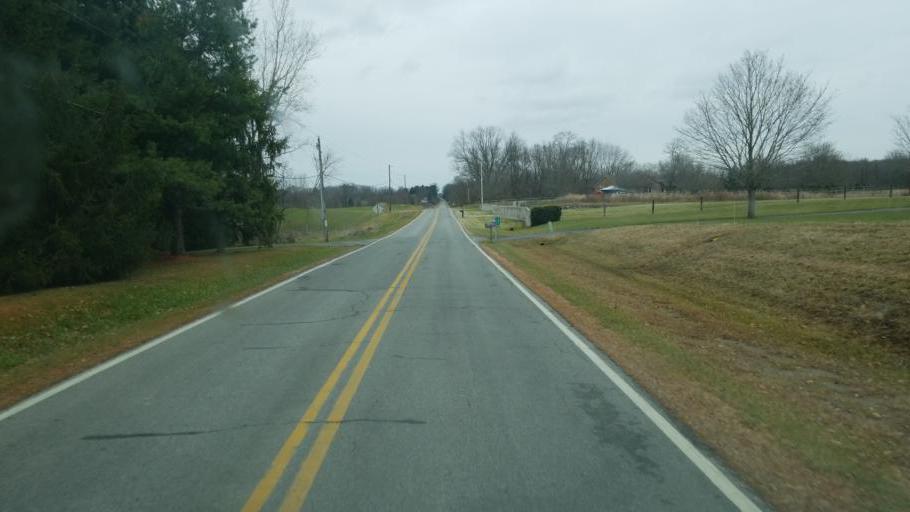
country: US
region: Ohio
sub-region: Delaware County
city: Delaware
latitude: 40.3003
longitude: -82.9621
